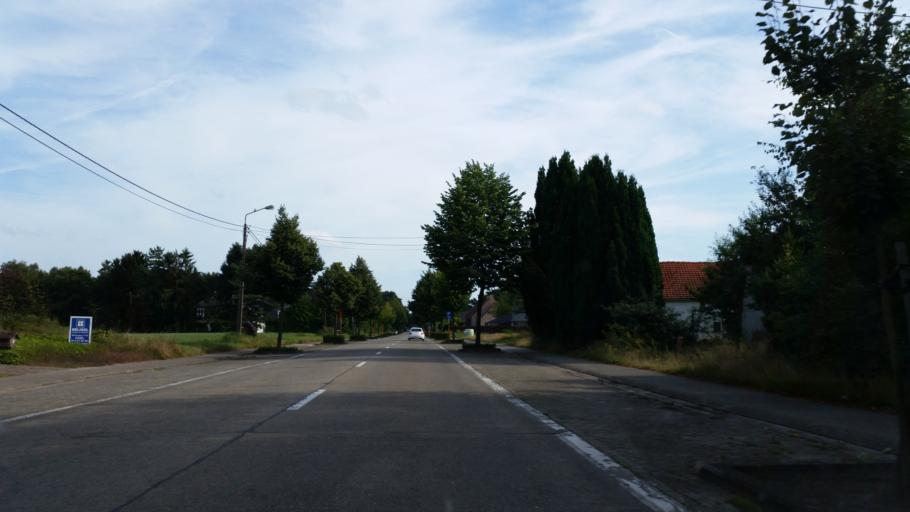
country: BE
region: Flanders
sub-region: Provincie Antwerpen
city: Westerlo
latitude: 51.0990
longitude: 4.9183
